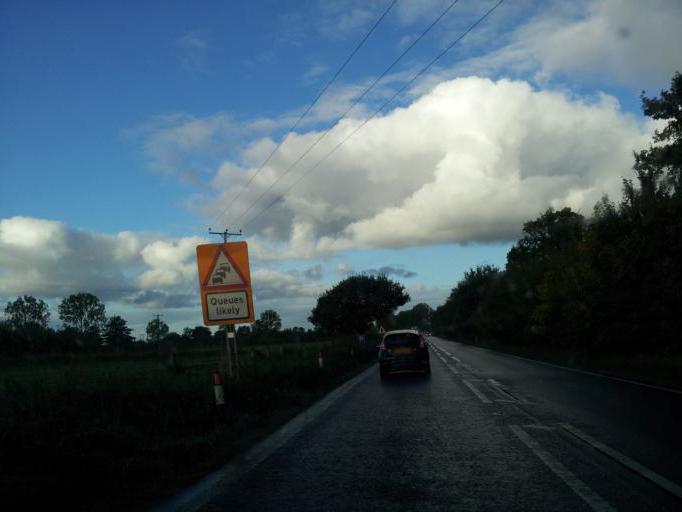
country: GB
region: England
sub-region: Norfolk
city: Lingwood
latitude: 52.6354
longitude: 1.4966
